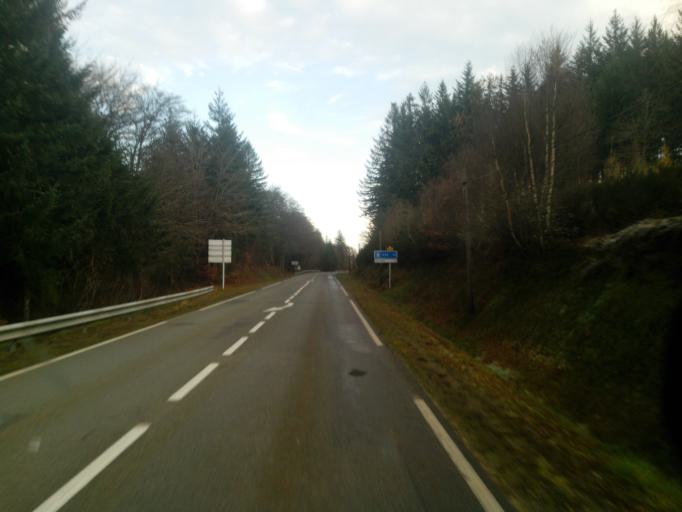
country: FR
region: Limousin
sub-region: Departement de la Correze
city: Meymac
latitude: 45.5802
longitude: 2.1304
